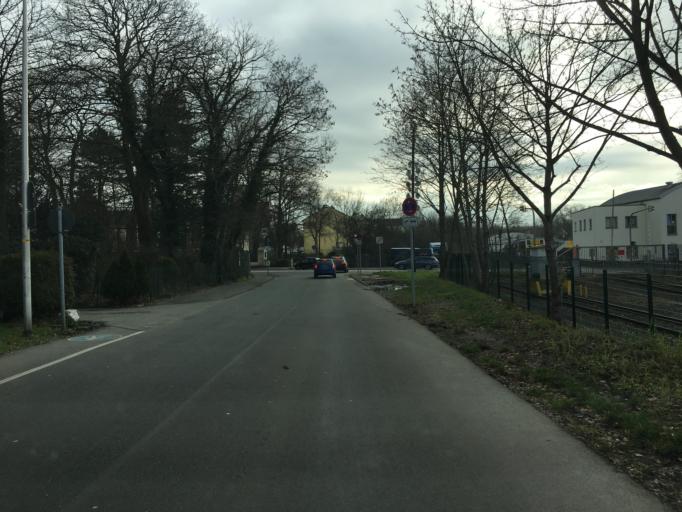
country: DE
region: North Rhine-Westphalia
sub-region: Regierungsbezirk Koln
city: Leverkusen
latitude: 51.0020
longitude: 6.9809
